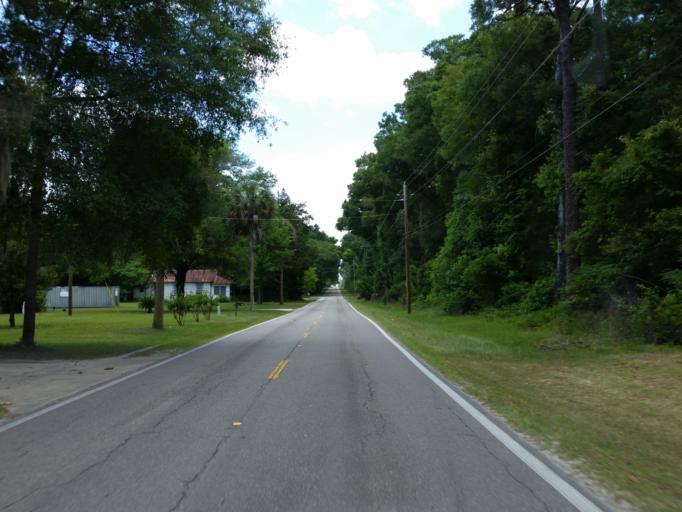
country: US
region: Florida
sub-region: Marion County
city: Belleview
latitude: 29.0113
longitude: -82.0763
